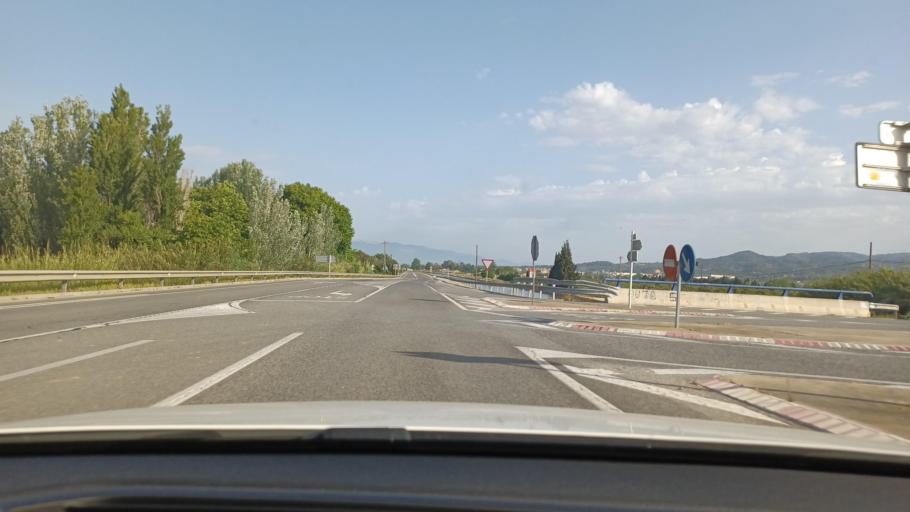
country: ES
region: Catalonia
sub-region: Provincia de Tarragona
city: Amposta
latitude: 40.7424
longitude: 0.5632
